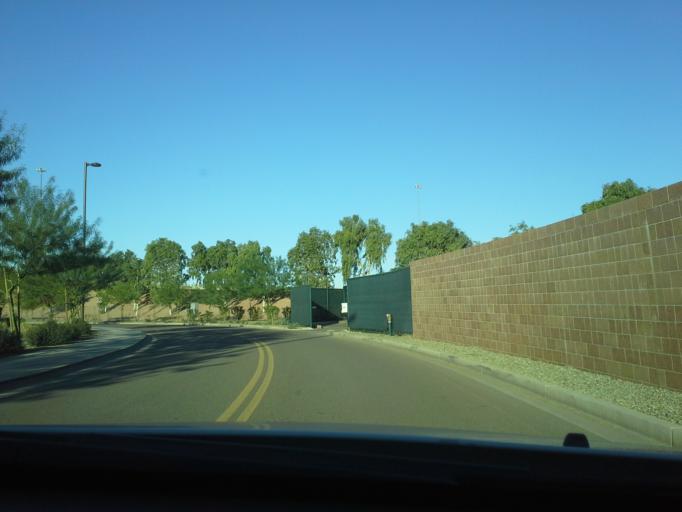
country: US
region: Arizona
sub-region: Maricopa County
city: Tempe
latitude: 33.4333
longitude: -111.8837
